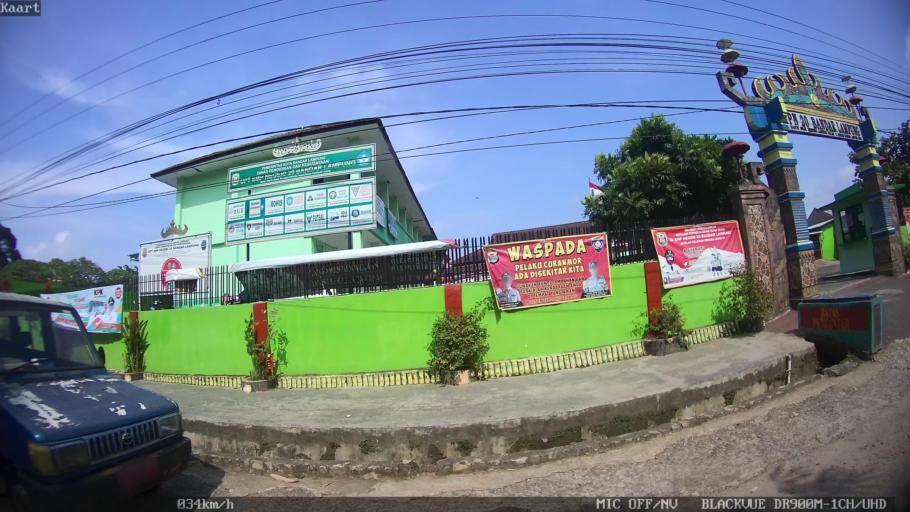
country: ID
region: Lampung
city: Kedaton
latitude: -5.3532
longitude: 105.2634
